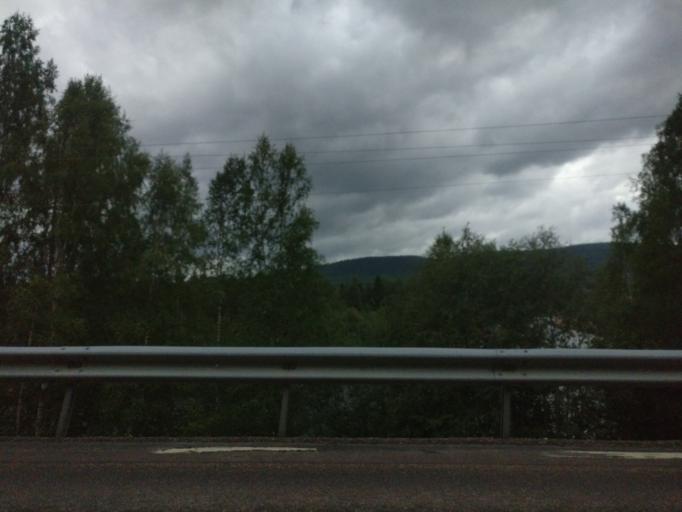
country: SE
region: Vaermland
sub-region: Torsby Kommun
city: Torsby
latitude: 60.5929
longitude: 13.0738
